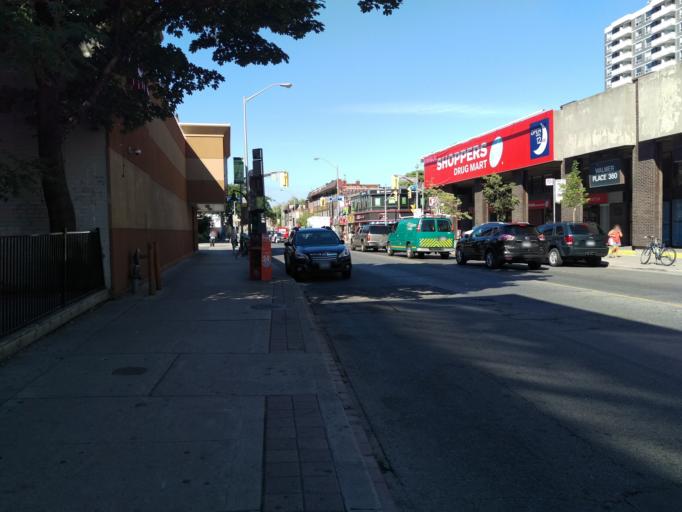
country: CA
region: Ontario
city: Toronto
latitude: 43.6665
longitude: -79.4047
